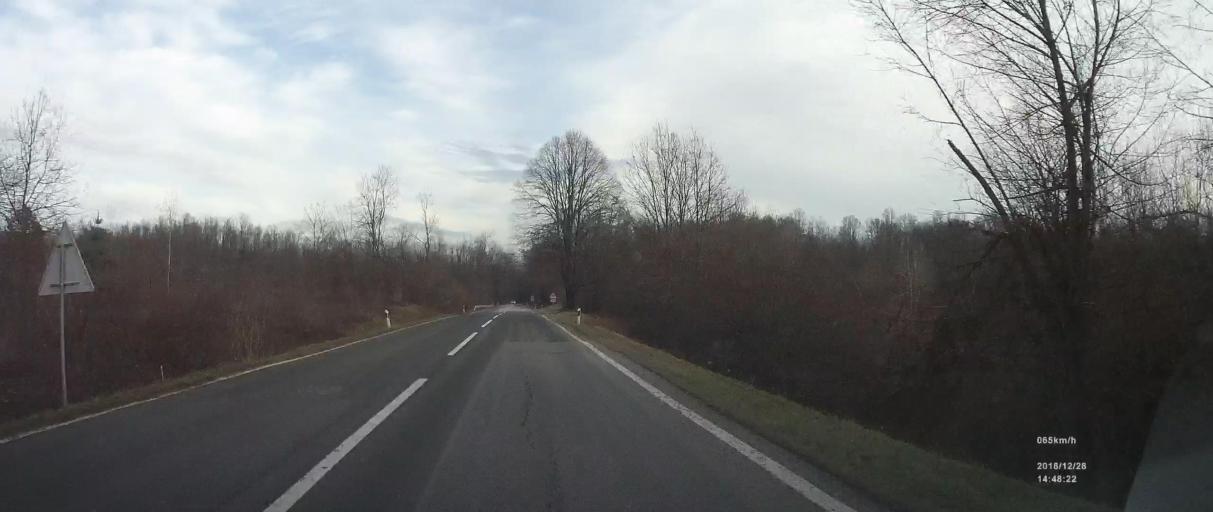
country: SI
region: Crnomelj
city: Crnomelj
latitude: 45.4459
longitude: 15.3393
